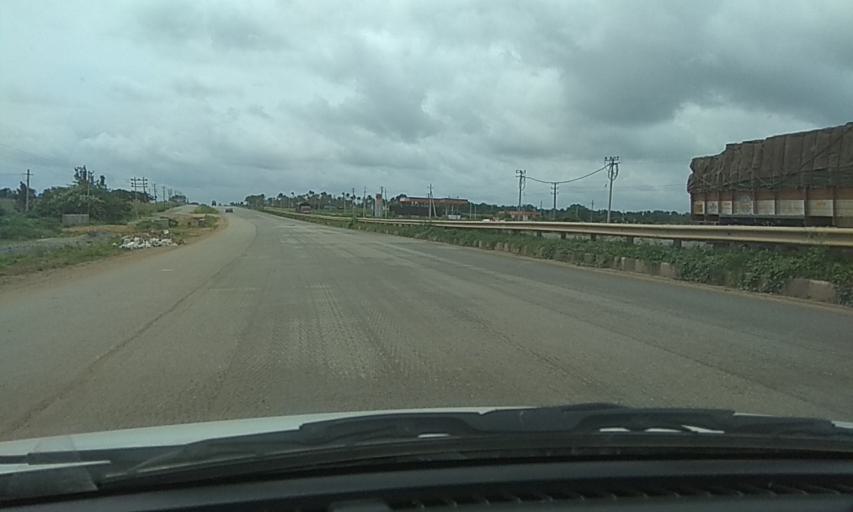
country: IN
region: Karnataka
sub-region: Davanagere
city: Mayakonda
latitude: 14.3585
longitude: 76.1982
